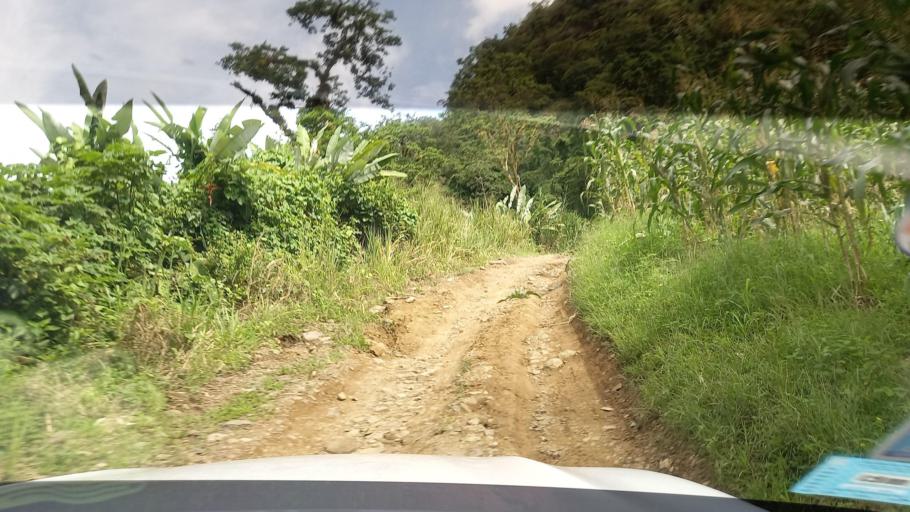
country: NI
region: Jinotega
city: San Jose de Bocay
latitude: 13.3992
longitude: -85.6979
